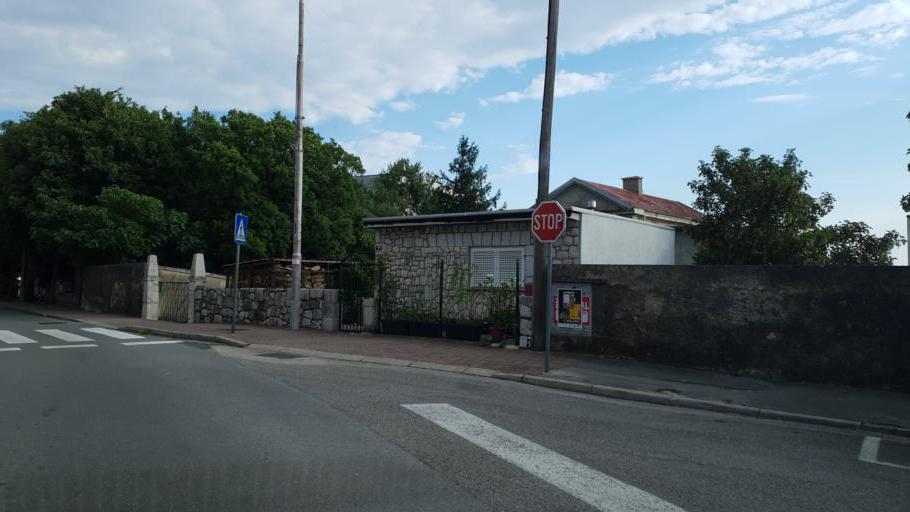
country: HR
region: Primorsko-Goranska
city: Kraljevica
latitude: 45.2757
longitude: 14.5688
